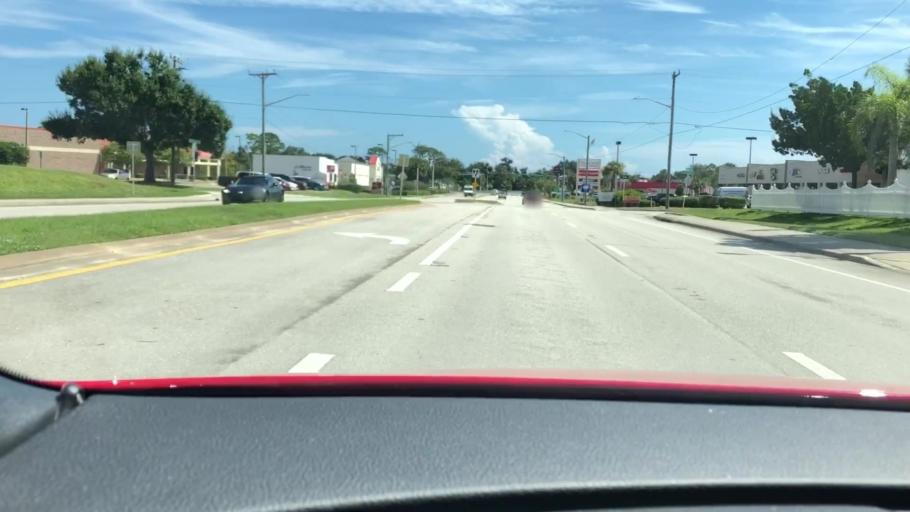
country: US
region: Florida
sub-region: Volusia County
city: Edgewater
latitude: 28.9715
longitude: -80.8987
